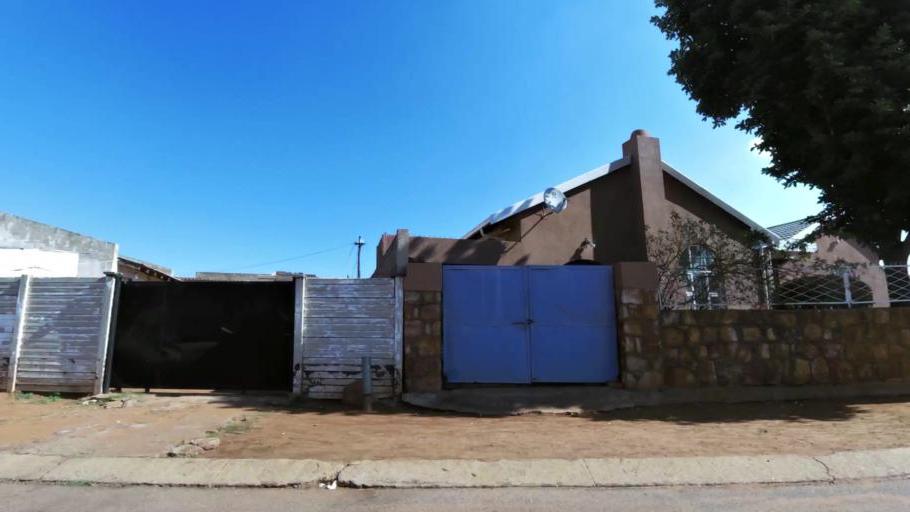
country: ZA
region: Gauteng
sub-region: City of Johannesburg Metropolitan Municipality
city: Soweto
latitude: -26.2354
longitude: 27.8863
